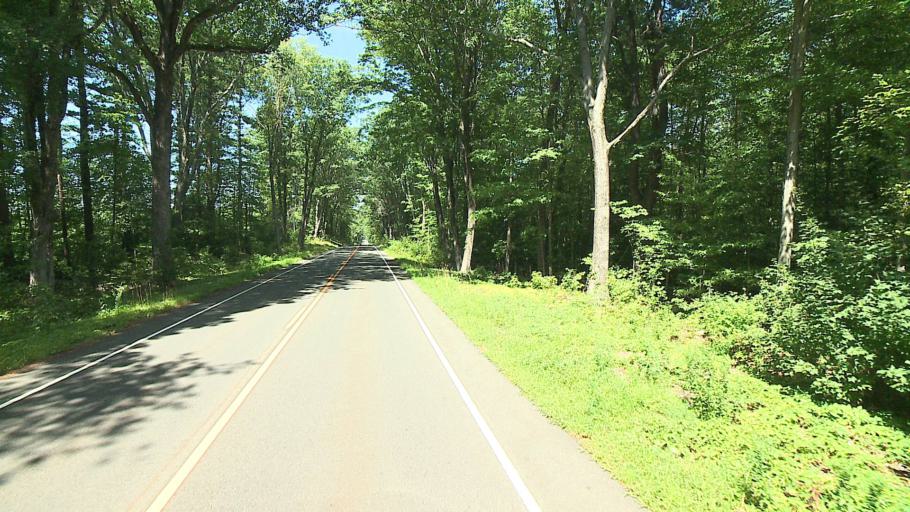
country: US
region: Connecticut
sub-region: Litchfield County
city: New Hartford Center
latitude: 41.9399
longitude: -72.9712
